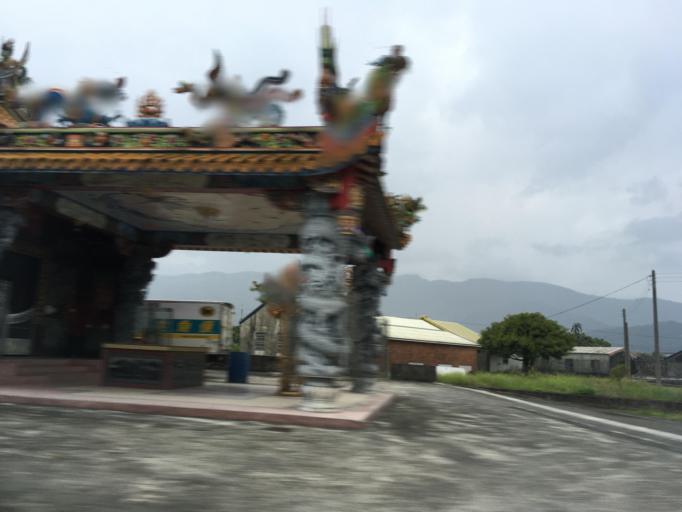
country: TW
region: Taiwan
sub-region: Yilan
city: Yilan
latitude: 24.6771
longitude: 121.6543
